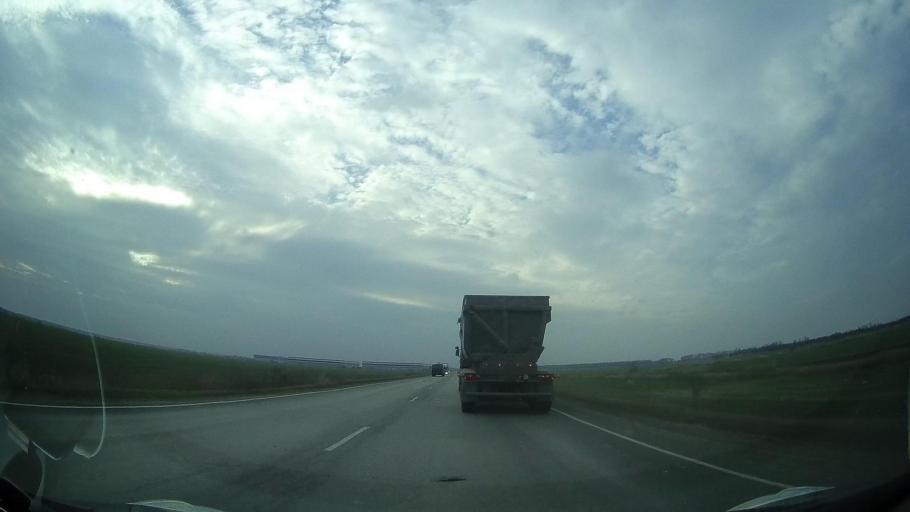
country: RU
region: Rostov
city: Ol'ginskaya
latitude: 47.1305
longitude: 39.9188
